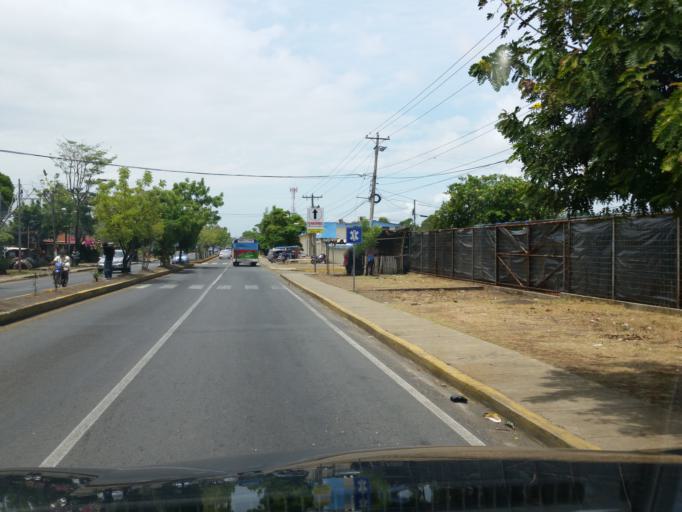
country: NI
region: Masaya
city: Masaya
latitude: 11.9910
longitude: -86.1011
